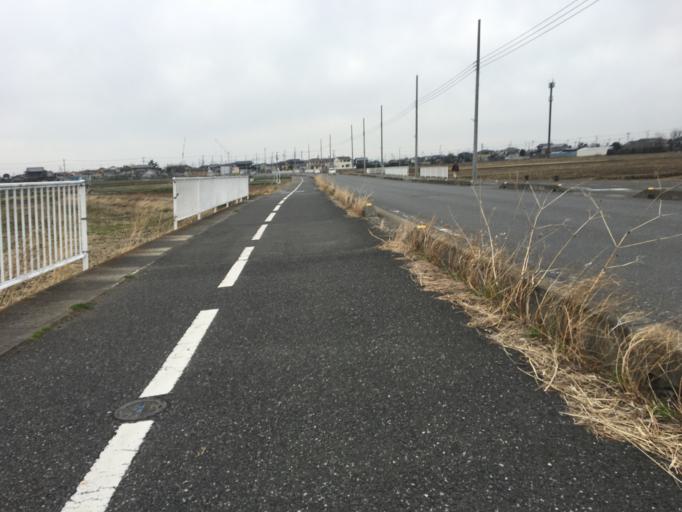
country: JP
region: Saitama
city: Kisai
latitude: 36.1081
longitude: 139.5846
